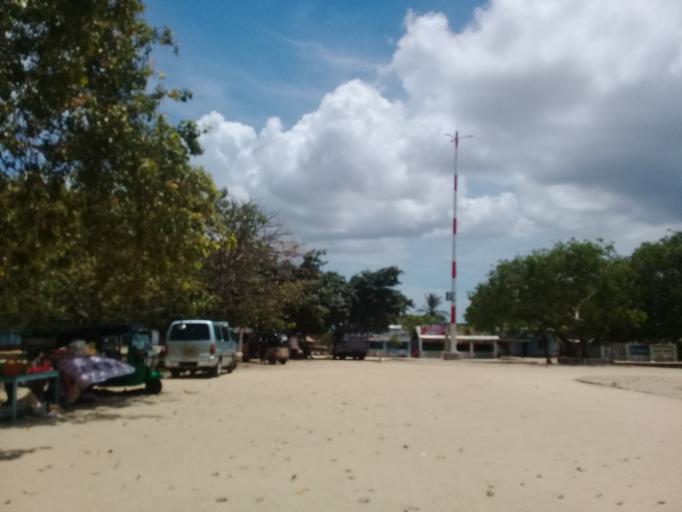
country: LK
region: Northern Province
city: Point Pedro
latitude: 9.7893
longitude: 80.2429
